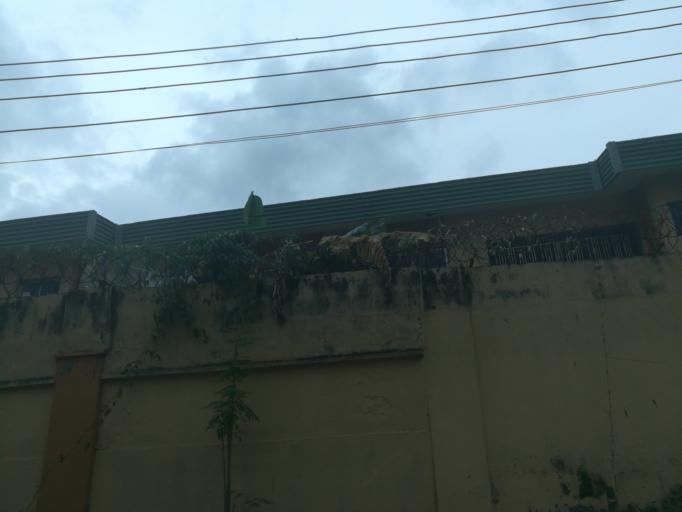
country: NG
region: Lagos
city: Ikeja
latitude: 6.6113
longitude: 3.3476
